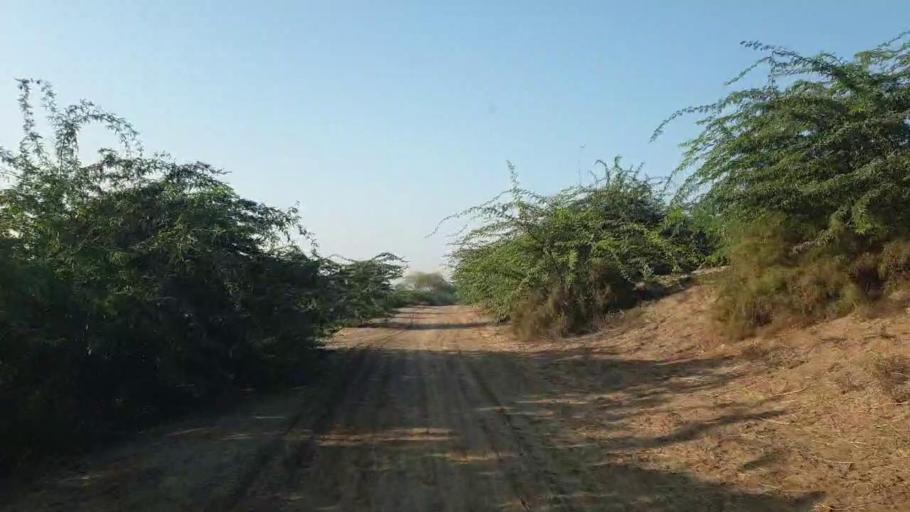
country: PK
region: Sindh
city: Badin
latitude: 24.6063
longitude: 68.7809
